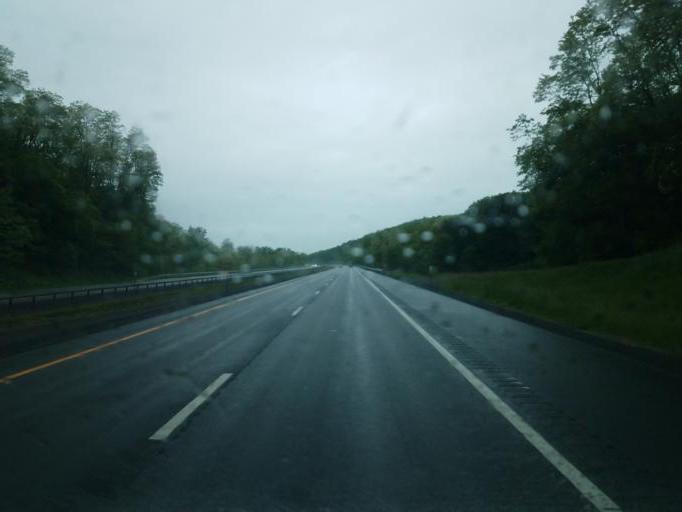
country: US
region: New York
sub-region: Herkimer County
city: Mohawk
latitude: 43.0214
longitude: -75.0188
